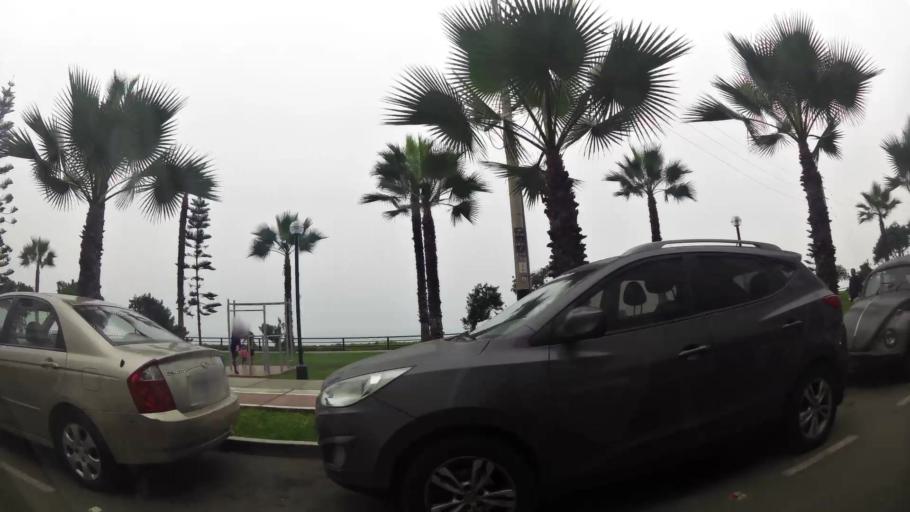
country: PE
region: Lima
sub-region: Lima
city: San Isidro
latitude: -12.1122
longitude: -77.0505
